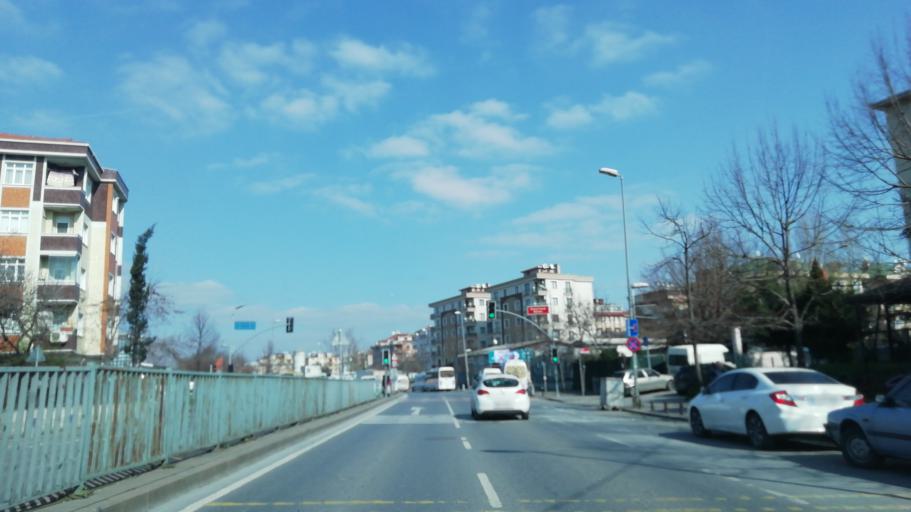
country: TR
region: Istanbul
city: Bahcelievler
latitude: 41.0078
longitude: 28.8472
